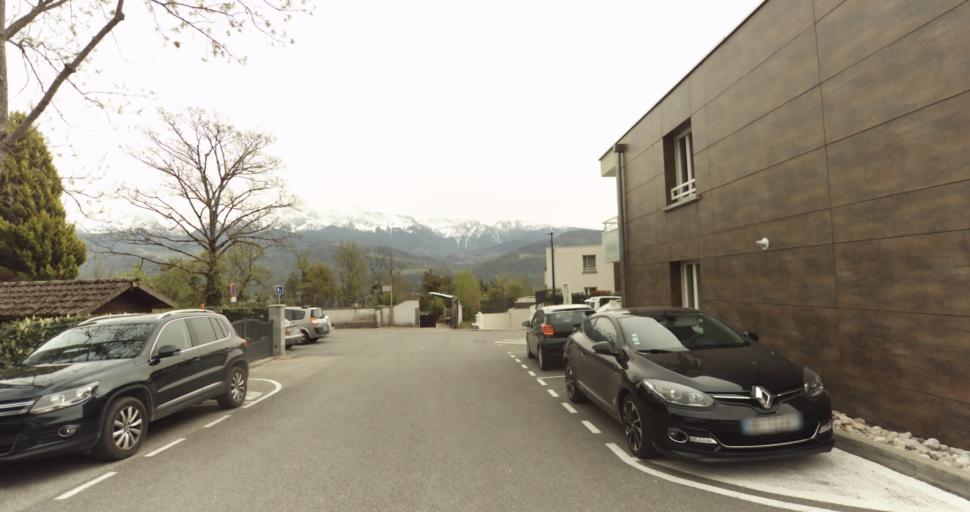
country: FR
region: Rhone-Alpes
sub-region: Departement de l'Isere
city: Montbonnot-Saint-Martin
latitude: 45.2279
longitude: 5.8050
